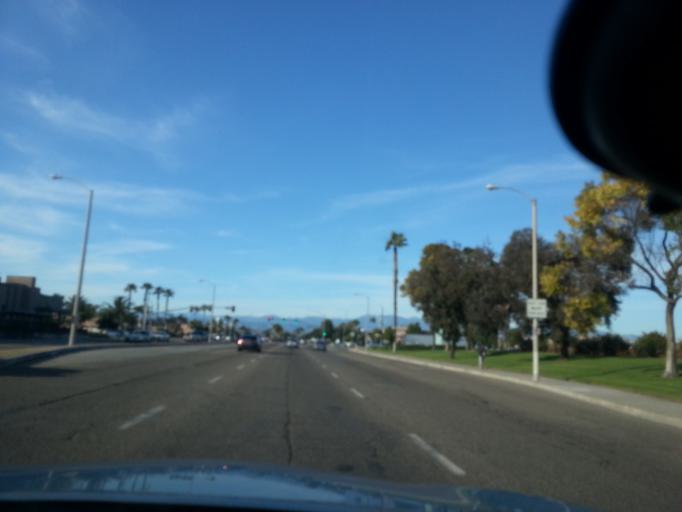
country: US
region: California
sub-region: Ventura County
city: El Rio
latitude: 34.2175
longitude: -119.1582
